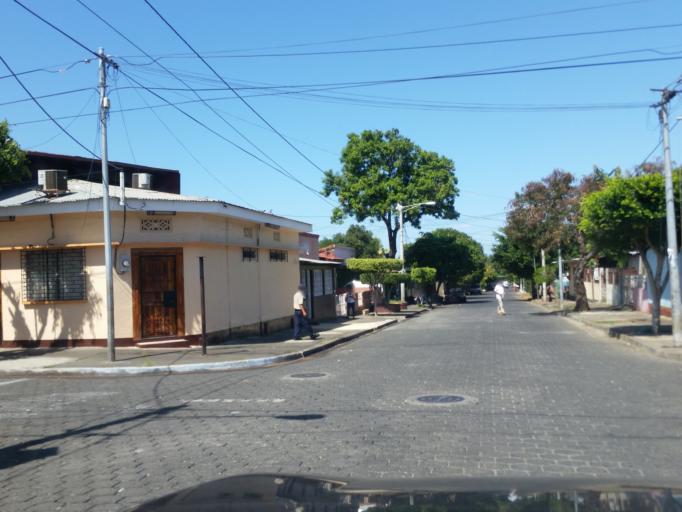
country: NI
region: Managua
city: Ciudad Sandino
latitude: 12.1510
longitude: -86.3001
